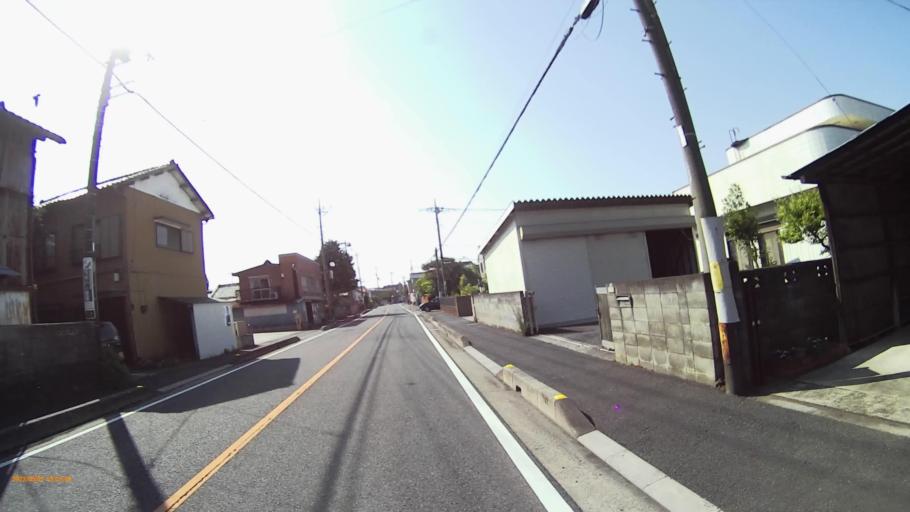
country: JP
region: Saitama
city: Sugito
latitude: 36.0237
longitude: 139.7389
